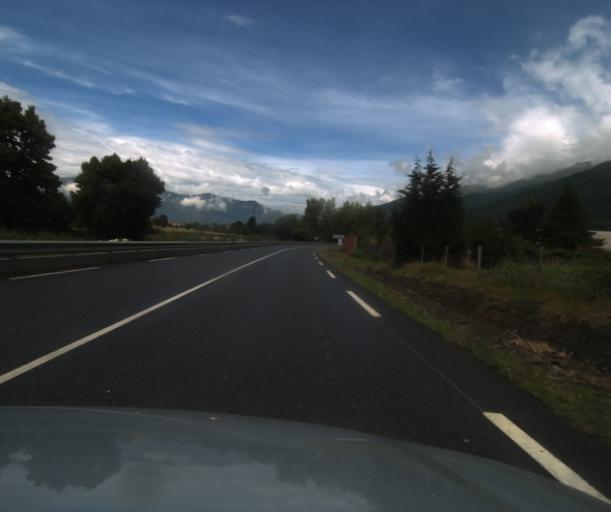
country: FR
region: Midi-Pyrenees
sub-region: Departement des Hautes-Pyrenees
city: Pierrefitte-Nestalas
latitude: 42.9562
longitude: -0.0657
